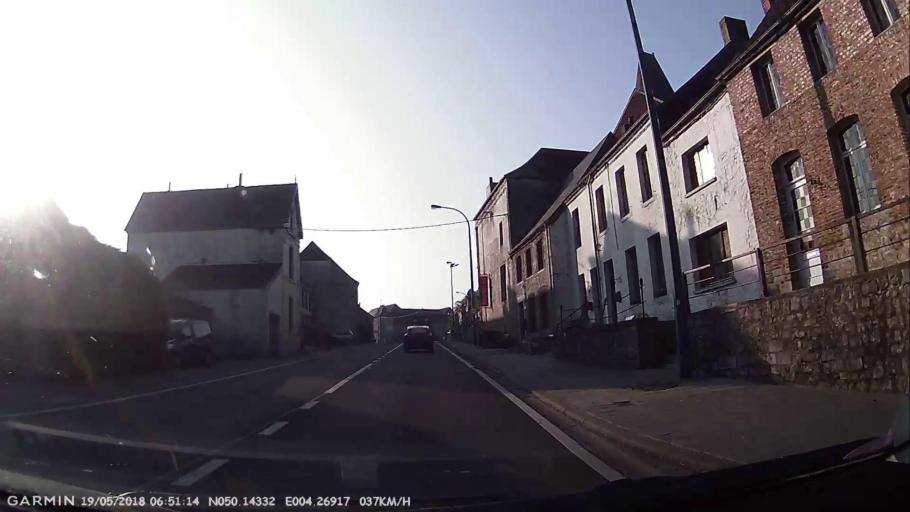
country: BE
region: Wallonia
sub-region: Province du Hainaut
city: Froidchapelle
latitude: 50.1433
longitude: 4.2694
